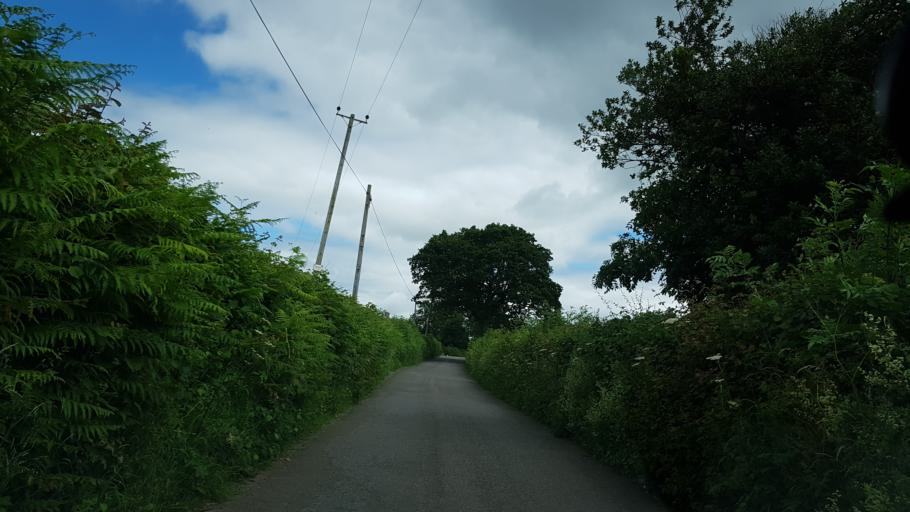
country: GB
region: Wales
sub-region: Monmouthshire
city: Llanarth
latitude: 51.7854
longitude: -2.8316
